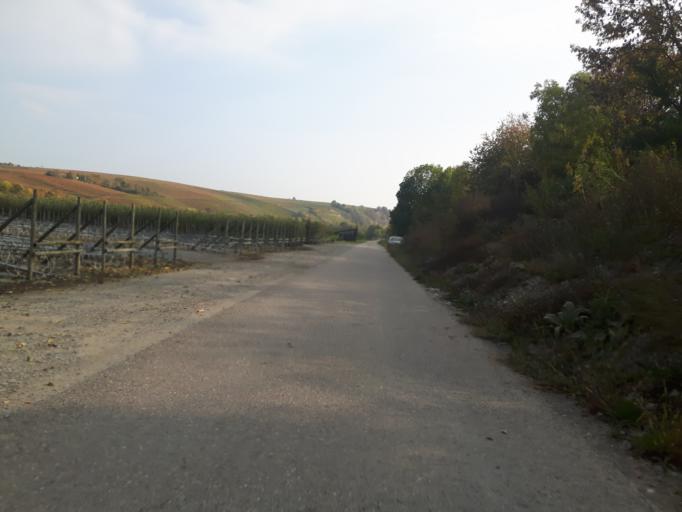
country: DE
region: Baden-Wuerttemberg
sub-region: Regierungsbezirk Stuttgart
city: Lauffen am Neckar
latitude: 49.0686
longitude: 9.1692
